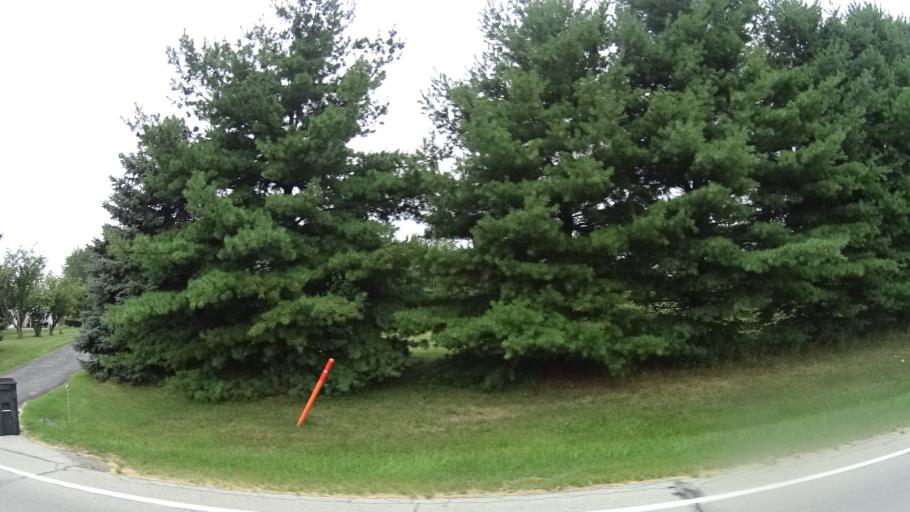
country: US
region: Indiana
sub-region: Madison County
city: Lapel
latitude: 40.0737
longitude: -85.8561
